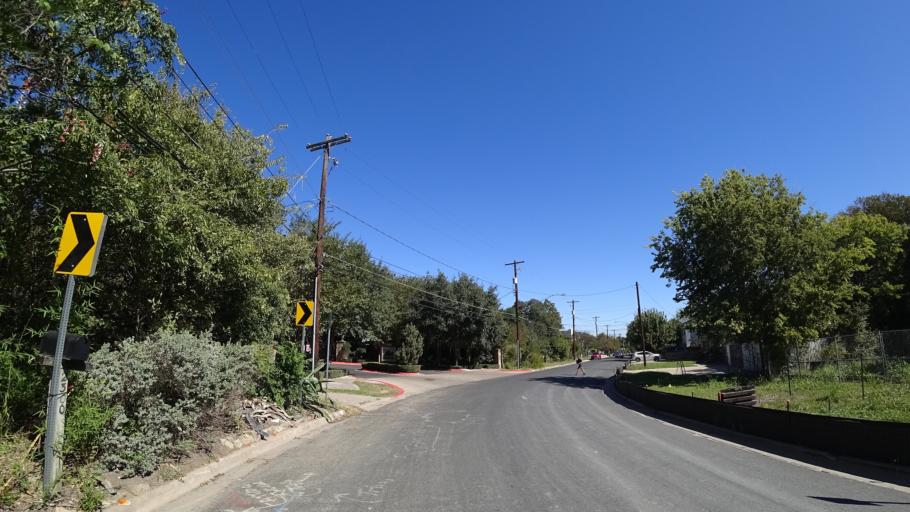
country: US
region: Texas
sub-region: Travis County
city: Austin
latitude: 30.2455
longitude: -97.7718
